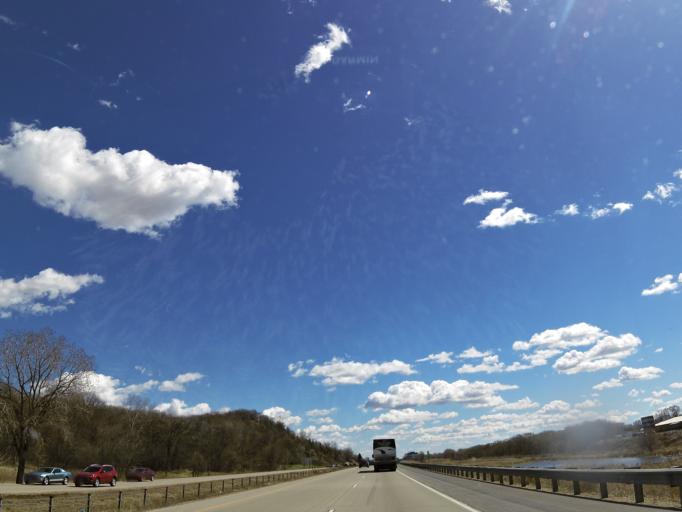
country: US
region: Minnesota
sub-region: Washington County
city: Saint Paul Park
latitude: 44.8422
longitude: -92.9768
